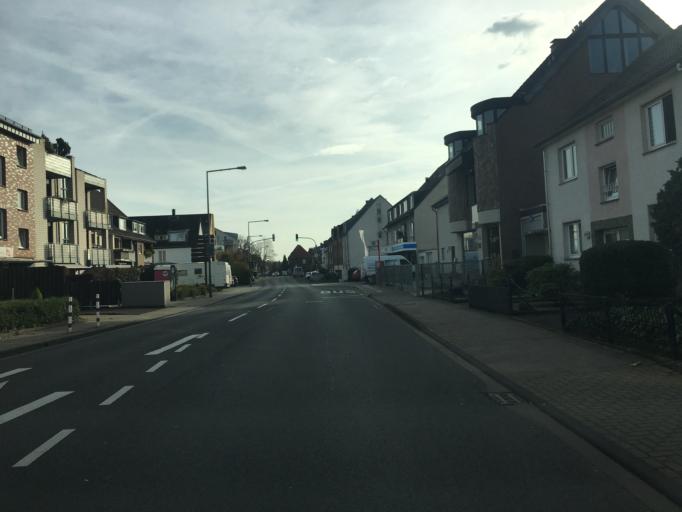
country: DE
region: North Rhine-Westphalia
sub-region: Regierungsbezirk Koln
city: Rath
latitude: 50.9454
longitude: 7.0812
